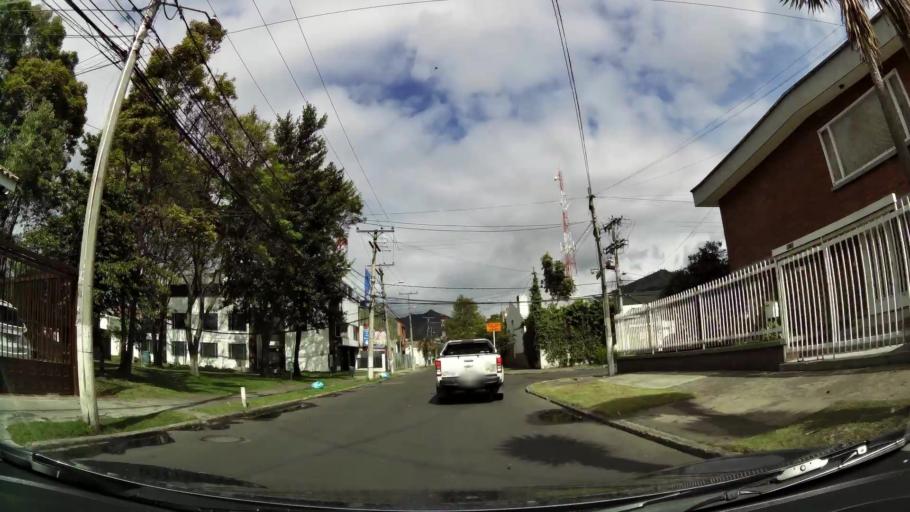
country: CO
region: Bogota D.C.
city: Barrio San Luis
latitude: 4.6896
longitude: -74.0599
